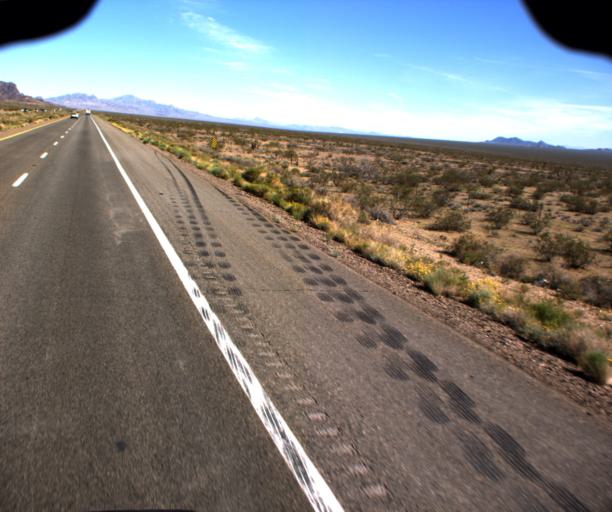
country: US
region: Arizona
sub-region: Mohave County
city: Dolan Springs
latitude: 35.7283
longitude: -114.4897
